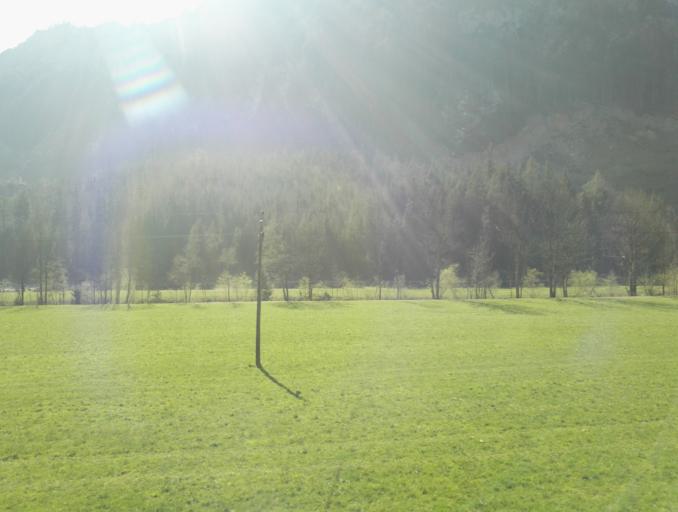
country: AT
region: Salzburg
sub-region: Politischer Bezirk Sankt Johann im Pongau
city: Forstau
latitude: 47.3930
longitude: 13.5112
